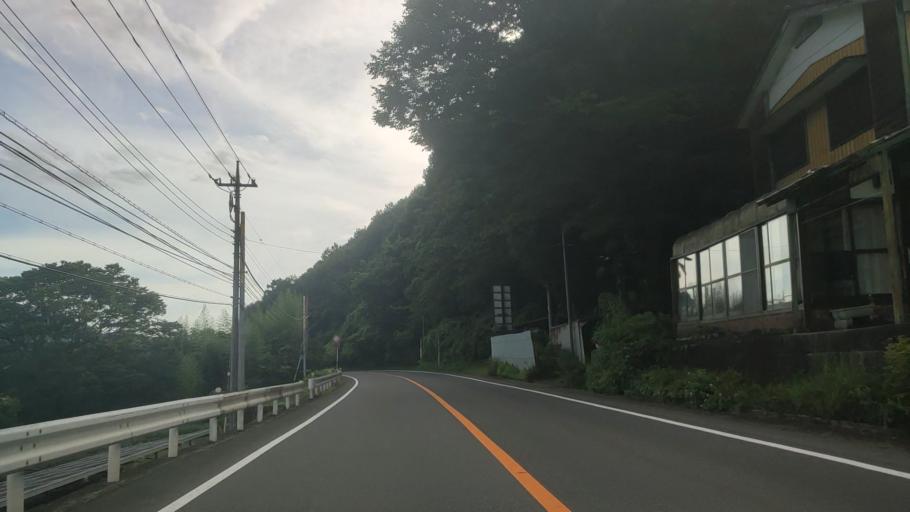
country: JP
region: Gunma
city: Omamacho-omama
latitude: 36.5300
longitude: 139.3225
